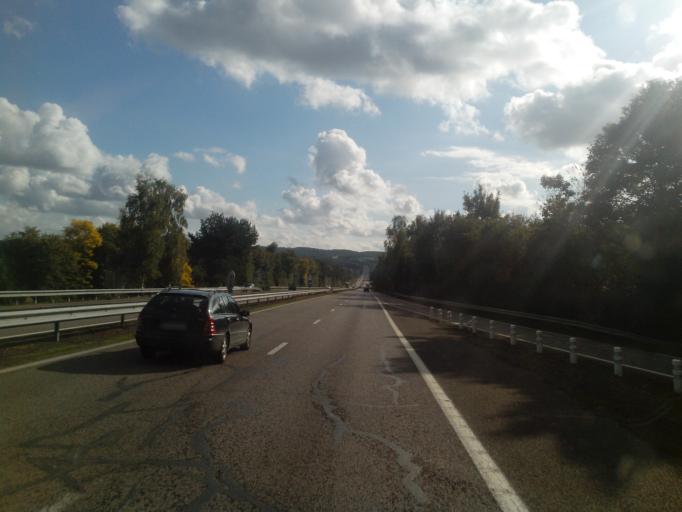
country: FR
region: Brittany
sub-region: Departement du Morbihan
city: Malestroit
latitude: 47.8505
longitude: -2.4206
